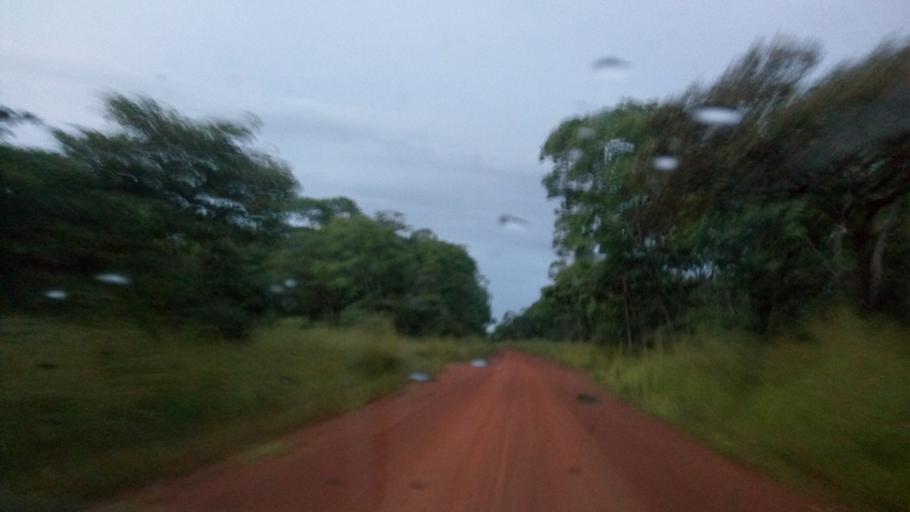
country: ZM
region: Luapula
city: Mwense
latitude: -9.8515
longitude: 28.1219
